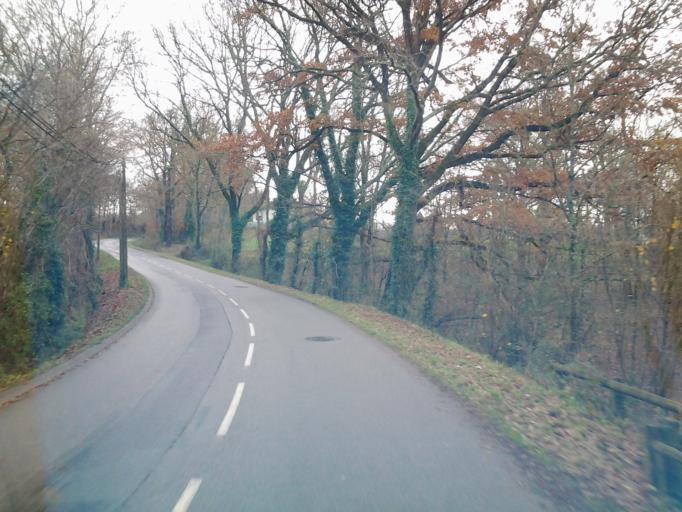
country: FR
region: Pays de la Loire
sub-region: Departement de la Vendee
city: La Roche-sur-Yon
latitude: 46.6590
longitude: -1.3982
